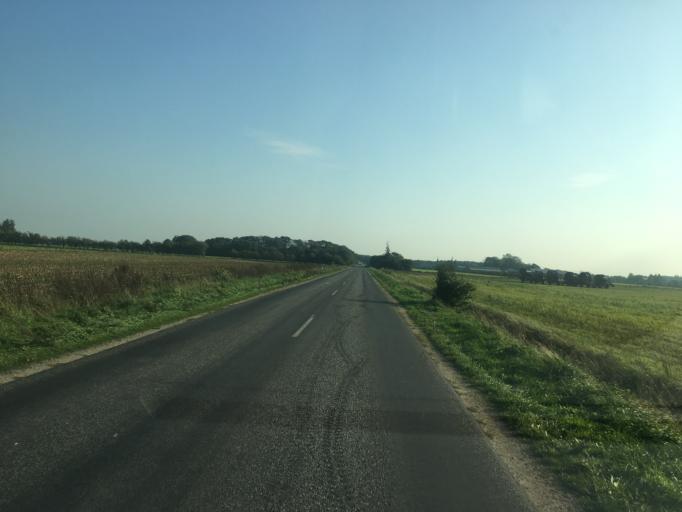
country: DE
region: Schleswig-Holstein
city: Bramstedtlund
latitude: 54.9375
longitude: 9.0668
